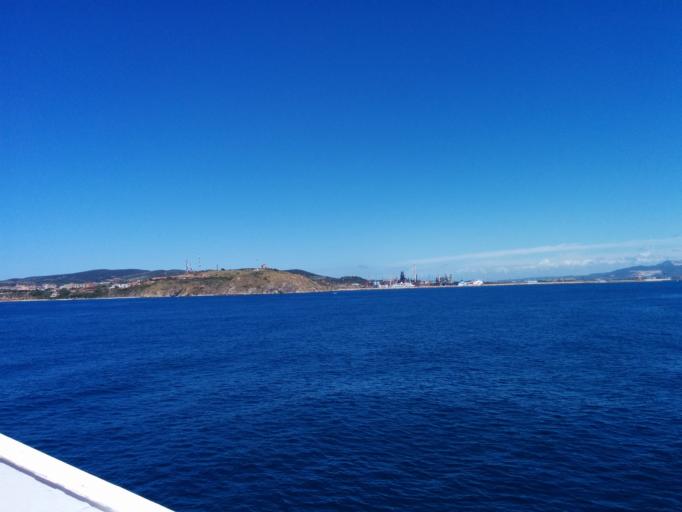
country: IT
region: Tuscany
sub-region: Provincia di Livorno
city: Piombino
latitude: 42.9086
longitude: 10.5511
